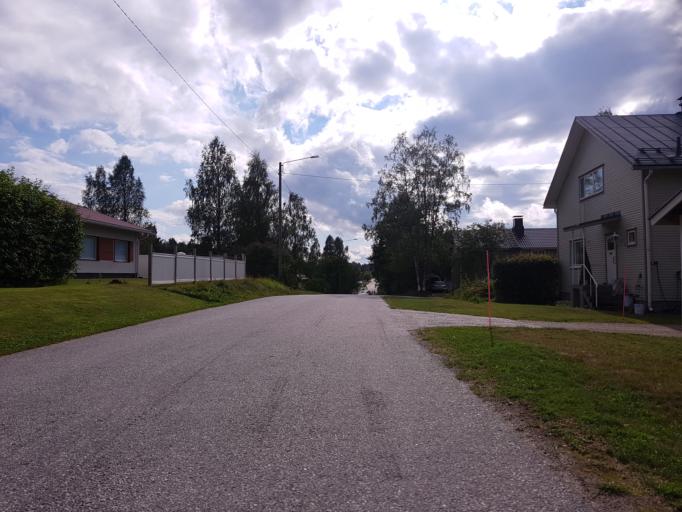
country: FI
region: Kainuu
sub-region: Kehys-Kainuu
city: Kuhmo
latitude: 64.1305
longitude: 29.5294
